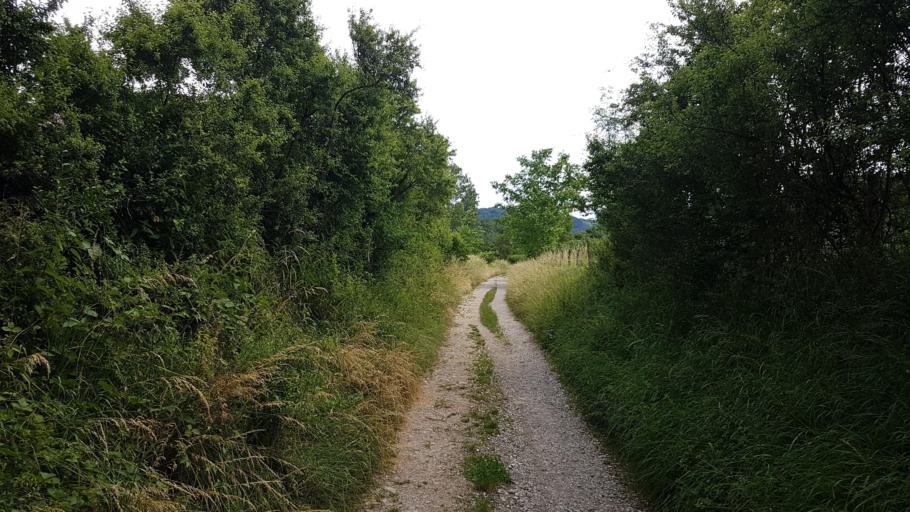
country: FR
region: Franche-Comte
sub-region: Departement du Jura
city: Perrigny
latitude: 46.6658
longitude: 5.5792
